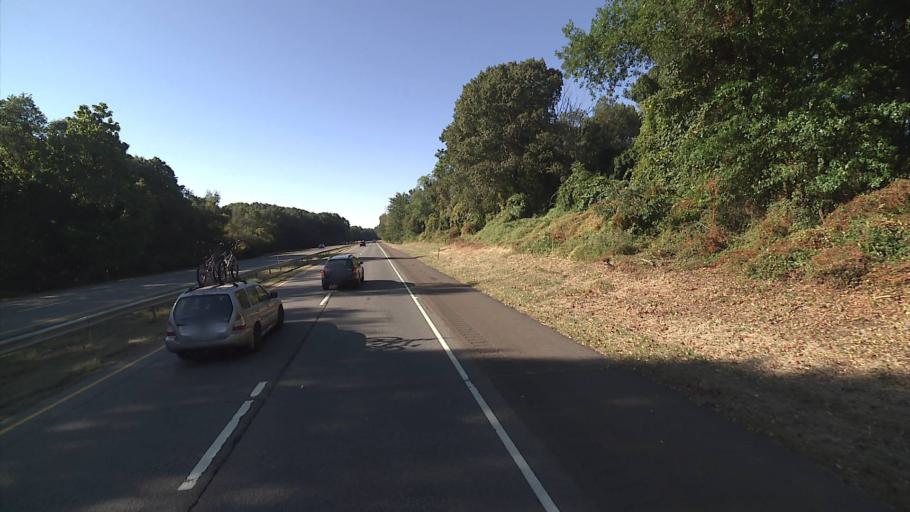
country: US
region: Connecticut
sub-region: New Haven County
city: North Haven
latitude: 41.4112
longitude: -72.8587
